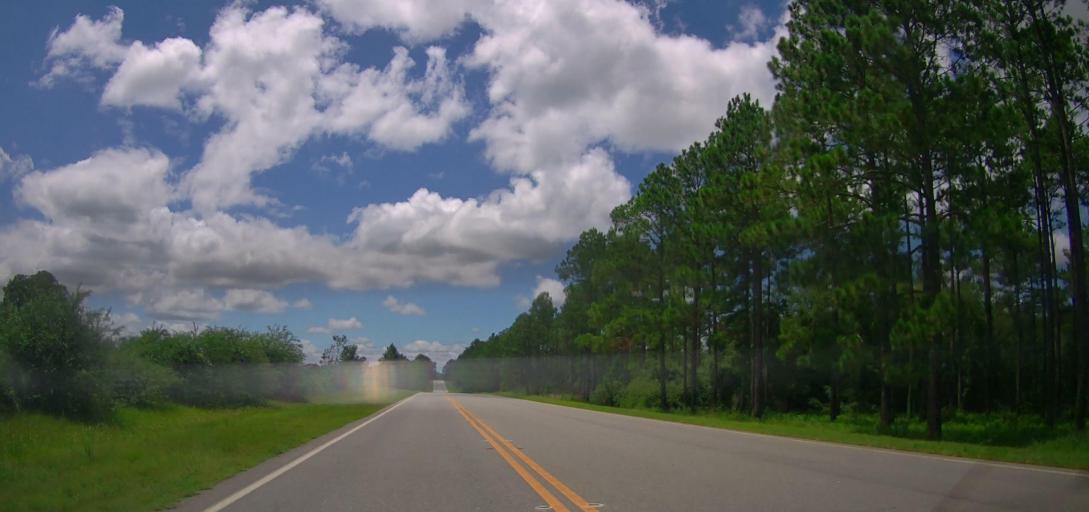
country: US
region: Georgia
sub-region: Turner County
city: Ashburn
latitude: 31.7223
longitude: -83.5595
